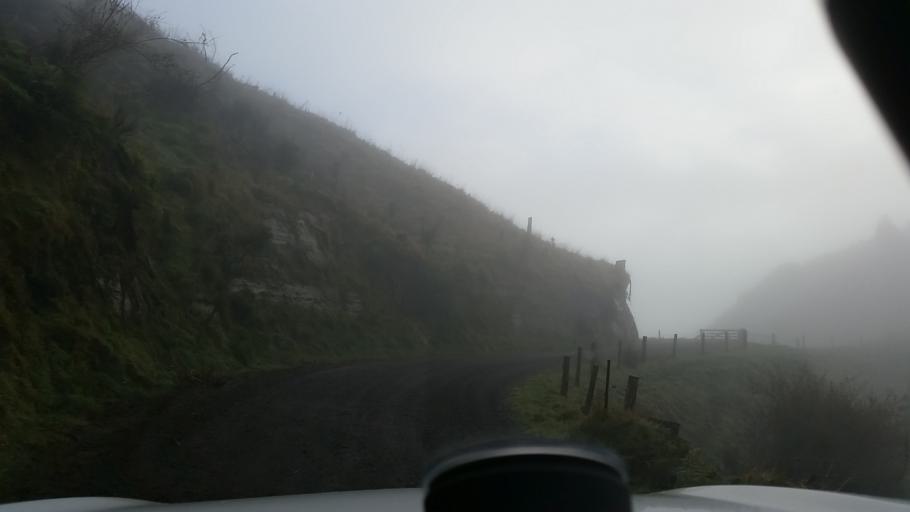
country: NZ
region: Taranaki
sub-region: South Taranaki District
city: Eltham
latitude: -39.4109
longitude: 174.4314
